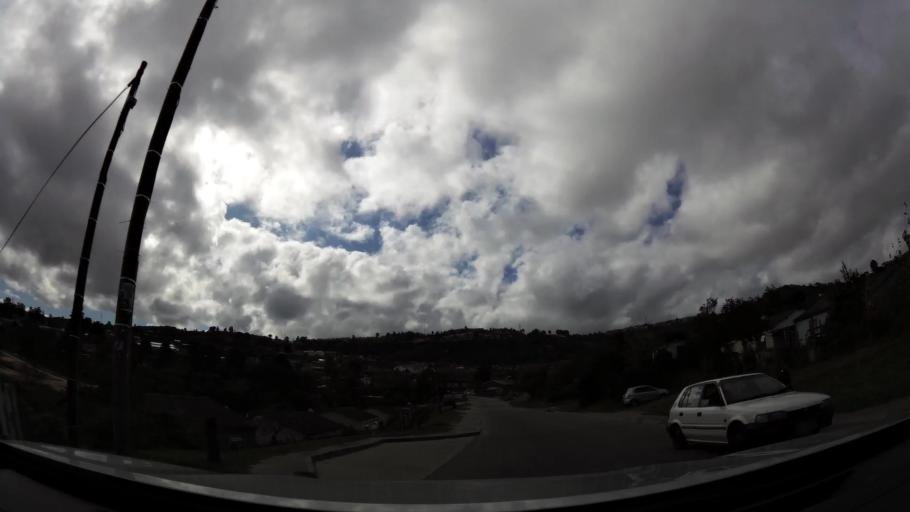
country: ZA
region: Western Cape
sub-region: Eden District Municipality
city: Knysna
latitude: -34.0502
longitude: 23.0963
